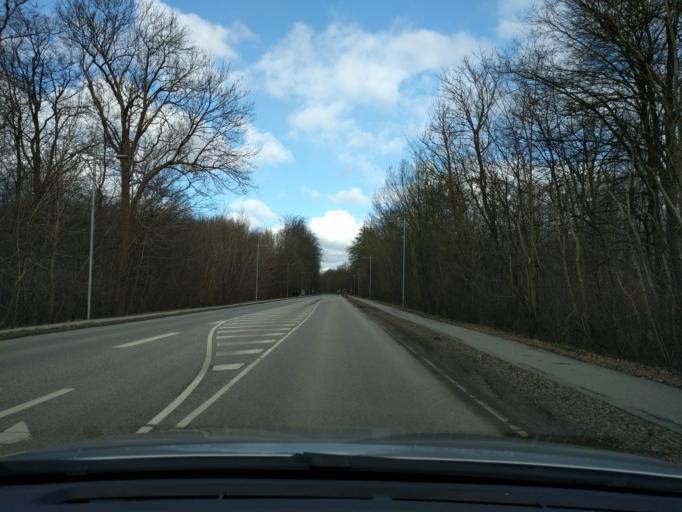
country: DK
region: Zealand
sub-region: Guldborgsund Kommune
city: Nykobing Falster
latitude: 54.7870
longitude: 11.8695
